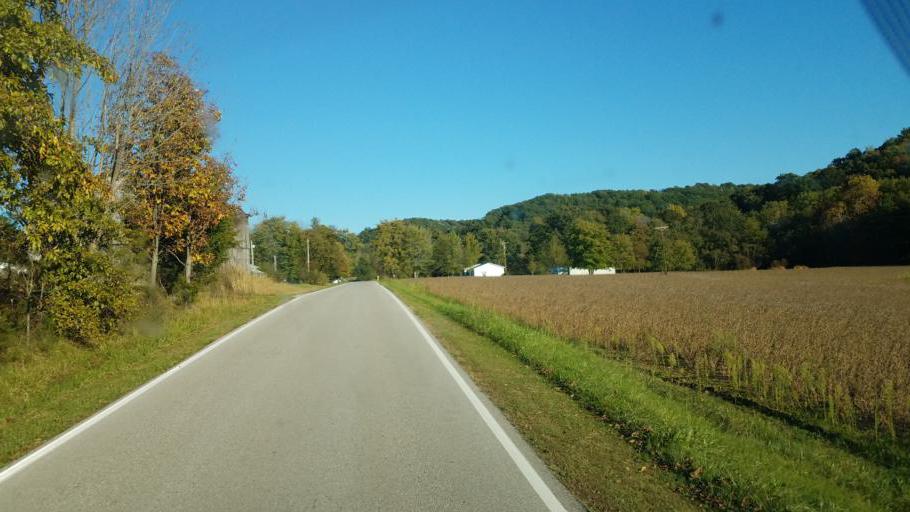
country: US
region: Ohio
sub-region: Adams County
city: Manchester
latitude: 38.5095
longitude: -83.5347
